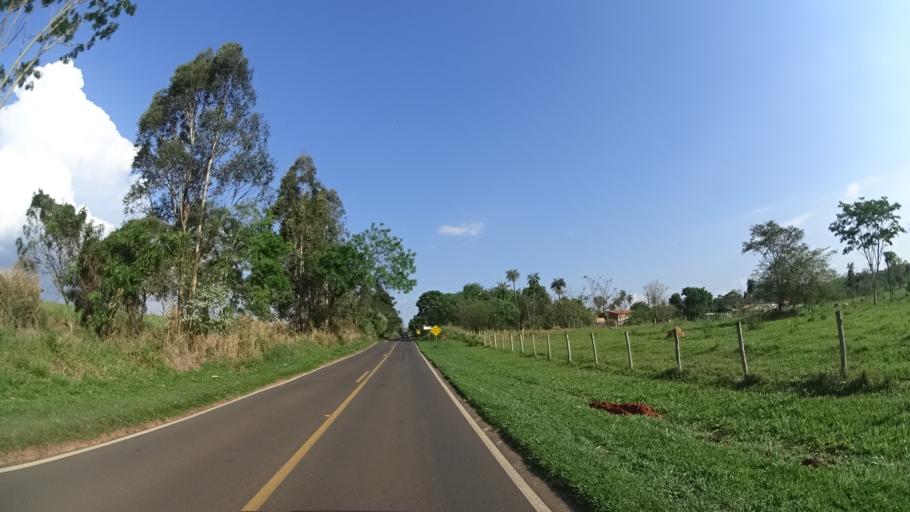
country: BR
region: Sao Paulo
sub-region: Urupes
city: Urupes
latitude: -21.3691
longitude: -49.4725
